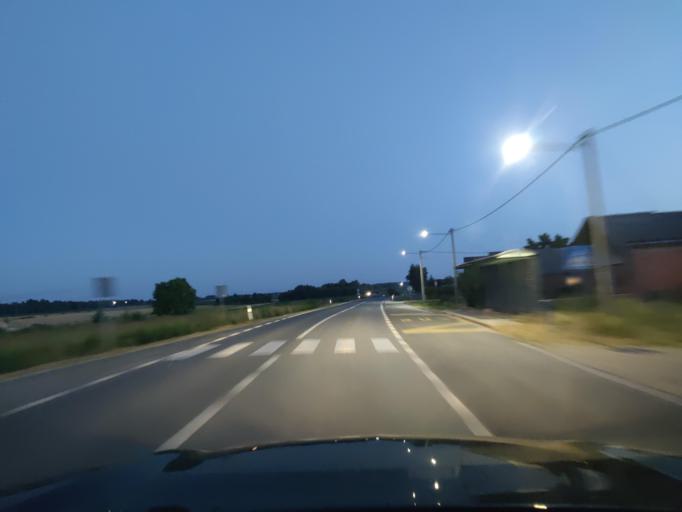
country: HR
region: Medimurska
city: Vratisinec
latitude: 46.4941
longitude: 16.4274
